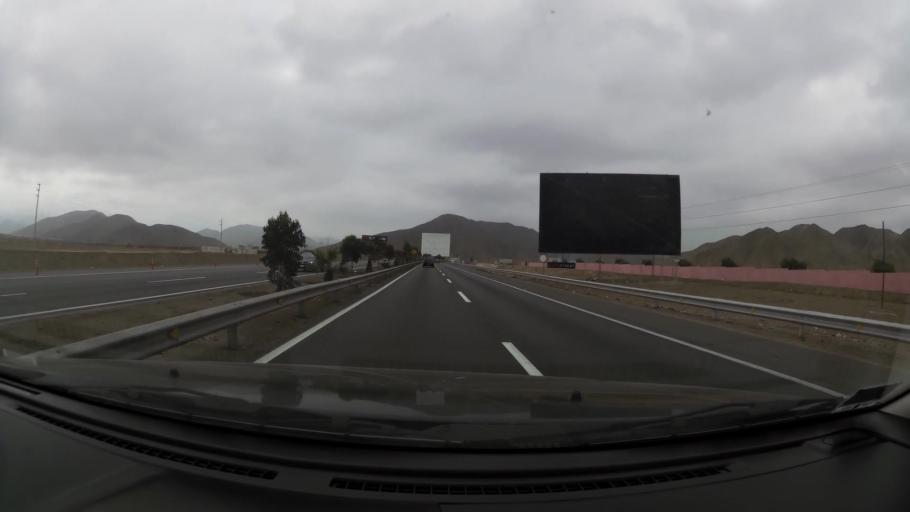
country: PE
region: Lima
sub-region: Lima
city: San Bartolo
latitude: -12.3957
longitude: -76.7594
